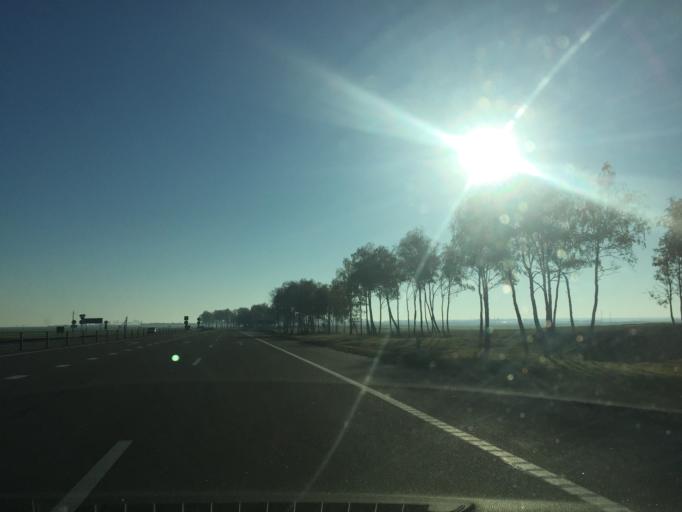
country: BY
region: Minsk
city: Luhavaya Slabada
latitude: 53.7628
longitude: 27.8749
